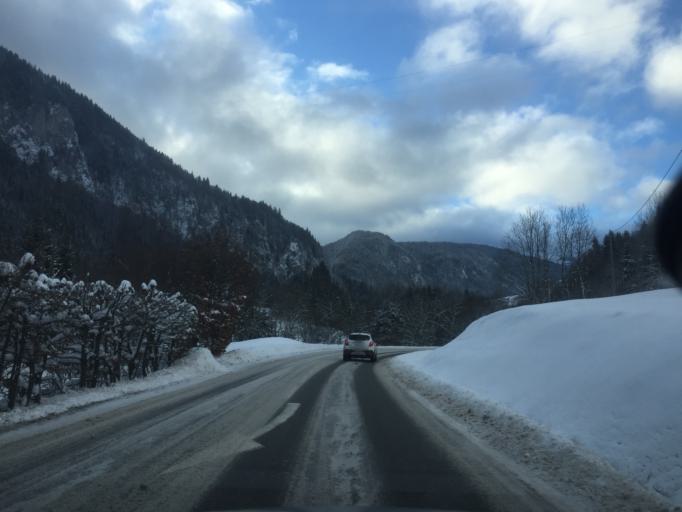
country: FR
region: Rhone-Alpes
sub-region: Departement de la Haute-Savoie
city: Abondance
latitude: 46.3102
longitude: 6.6781
